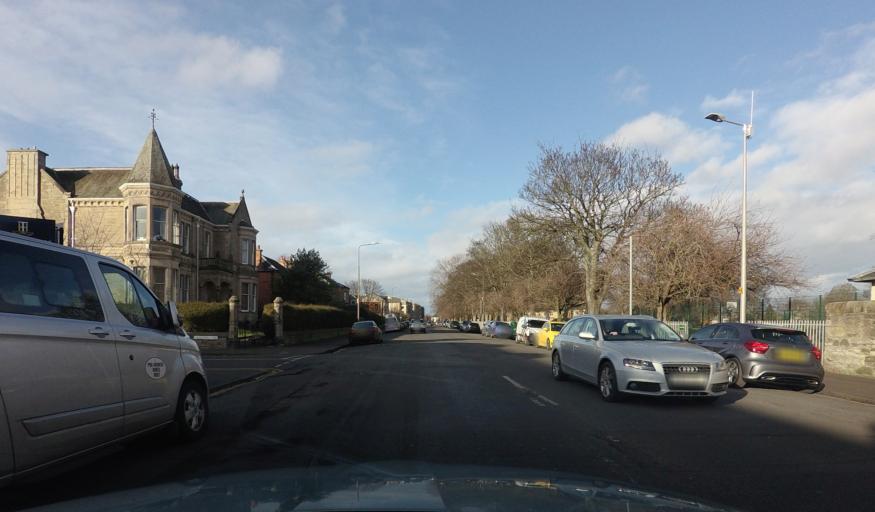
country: GB
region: Scotland
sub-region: Edinburgh
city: Edinburgh
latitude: 55.9739
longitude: -3.1957
